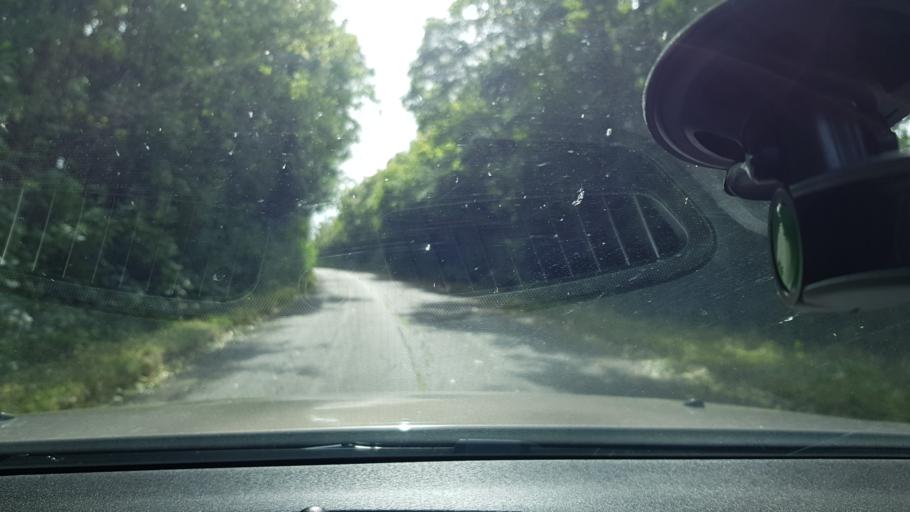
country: GB
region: England
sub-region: Wiltshire
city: Chilton Foliat
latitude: 51.4628
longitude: -1.5012
